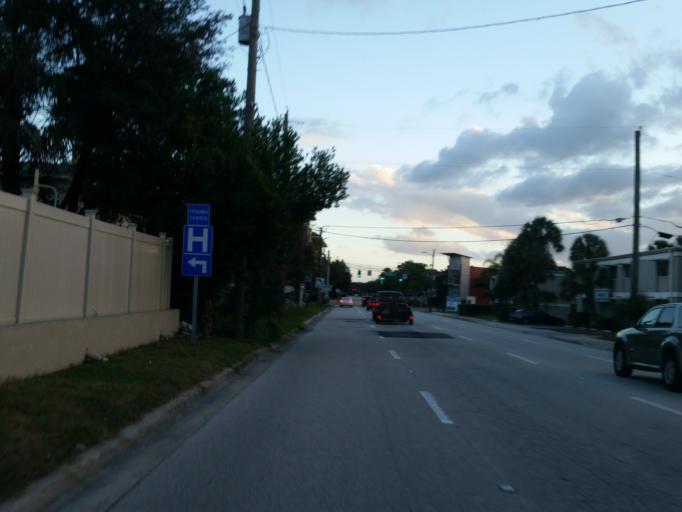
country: US
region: Florida
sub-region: Hillsborough County
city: Tampa
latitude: 27.9430
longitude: -82.4850
